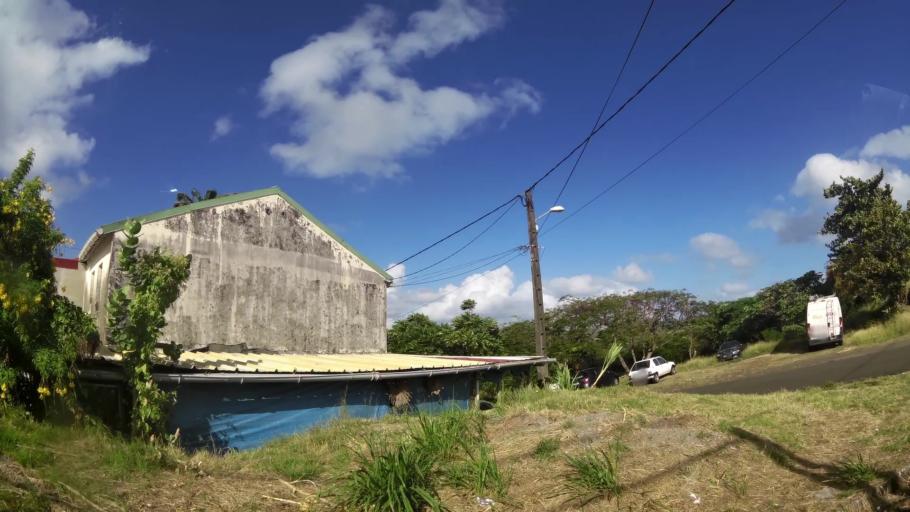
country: MQ
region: Martinique
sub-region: Martinique
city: Le Francois
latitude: 14.6185
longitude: -60.8885
